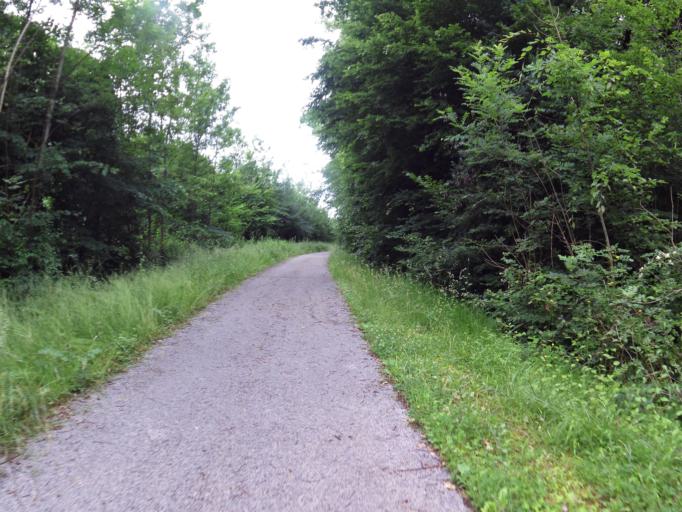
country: FR
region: Champagne-Ardenne
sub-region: Departement de la Haute-Marne
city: Montier-en-Der
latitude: 48.5376
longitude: 4.7694
